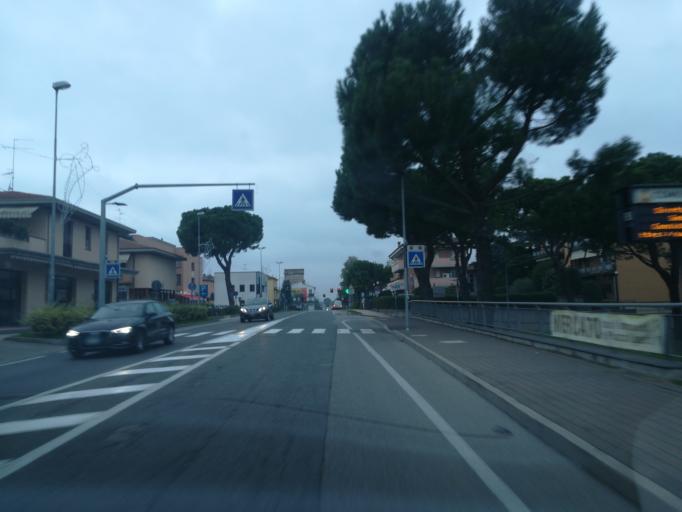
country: IT
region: Emilia-Romagna
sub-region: Provincia di Bologna
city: Toscanella
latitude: 44.3829
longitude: 11.6382
